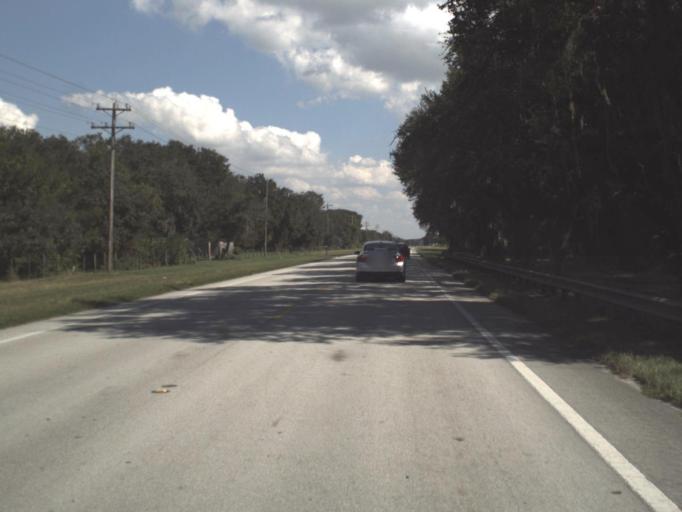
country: US
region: Florida
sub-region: Okeechobee County
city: Okeechobee
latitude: 27.3878
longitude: -81.0189
